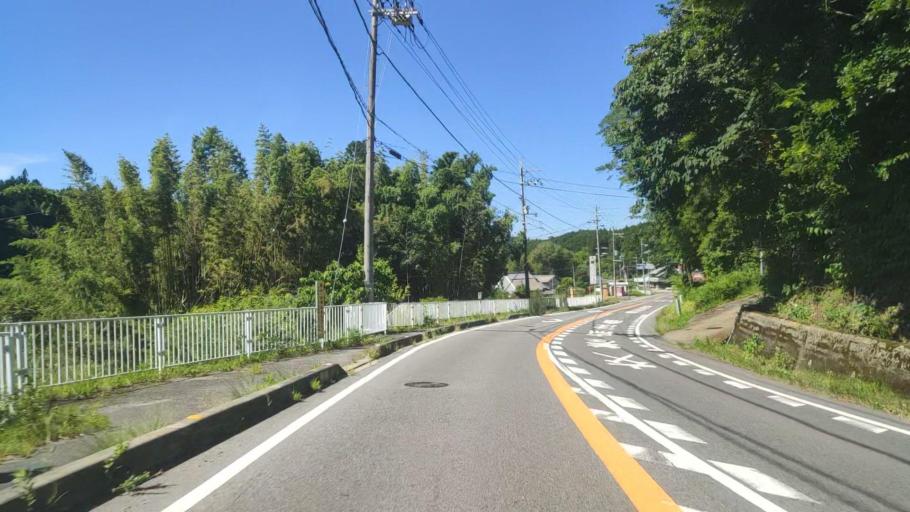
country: JP
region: Nara
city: Haibara-akanedai
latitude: 34.4624
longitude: 135.9331
